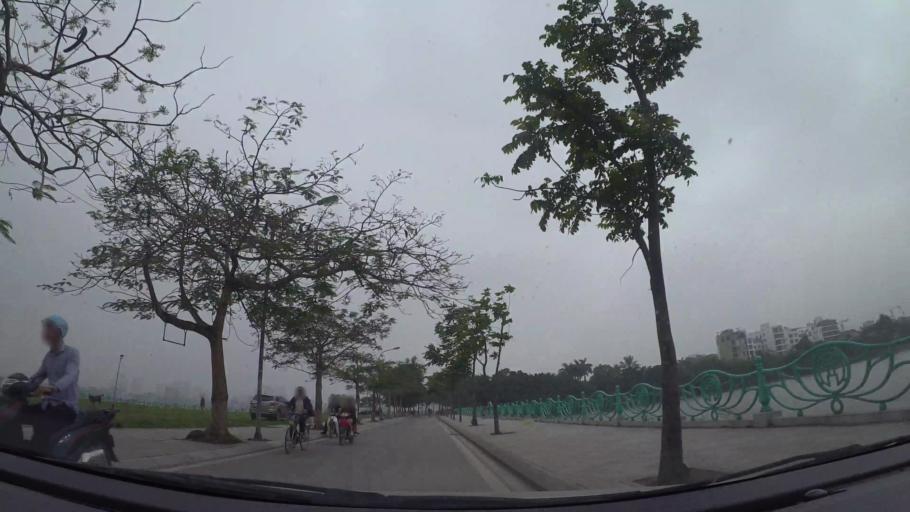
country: VN
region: Ha Noi
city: Tay Ho
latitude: 21.0583
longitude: 105.8193
